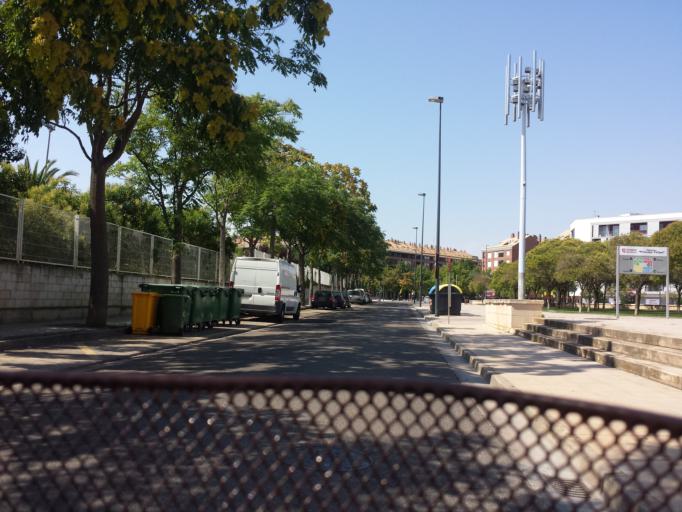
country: ES
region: Aragon
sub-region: Provincia de Zaragoza
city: Zaragoza
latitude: 41.6355
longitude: -0.8672
